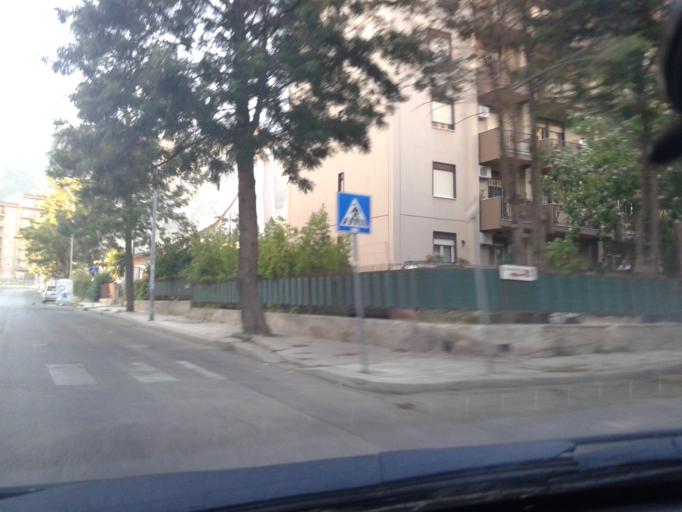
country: IT
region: Sicily
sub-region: Palermo
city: Ciaculli
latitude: 38.0856
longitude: 13.3617
